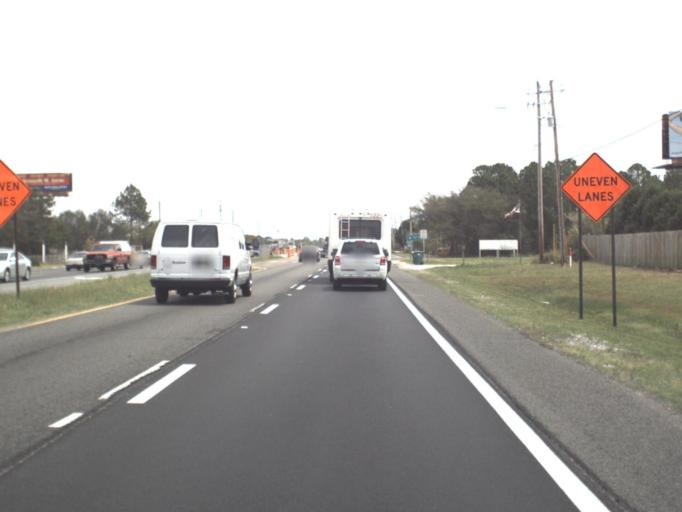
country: US
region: Florida
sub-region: Santa Rosa County
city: Navarre
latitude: 30.4096
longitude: -86.8302
